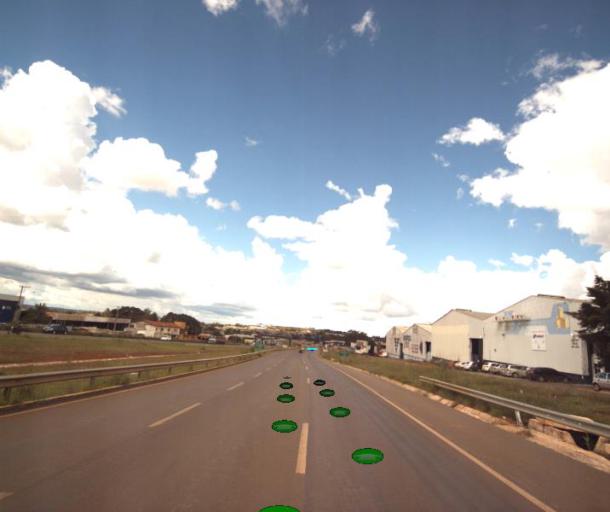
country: BR
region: Goias
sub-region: Anapolis
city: Anapolis
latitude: -16.3533
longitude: -48.9196
